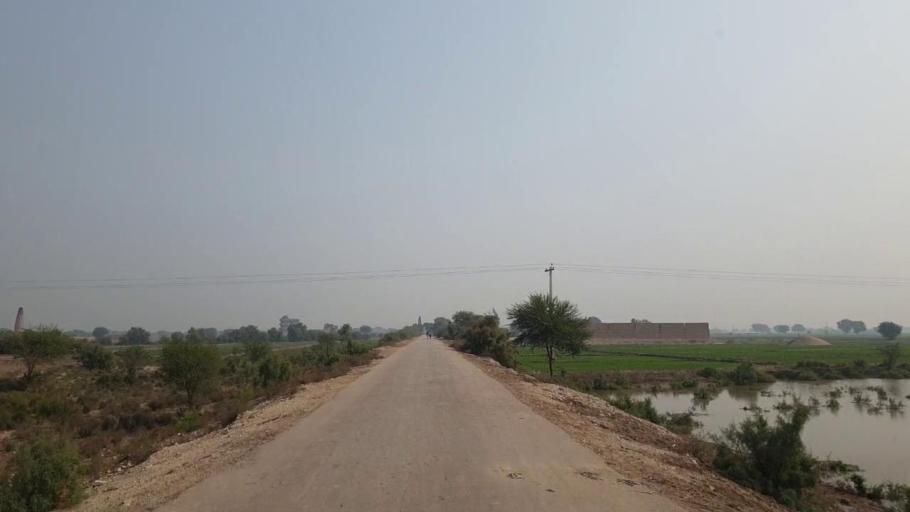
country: PK
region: Sindh
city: Bhan
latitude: 26.5165
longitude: 67.7213
